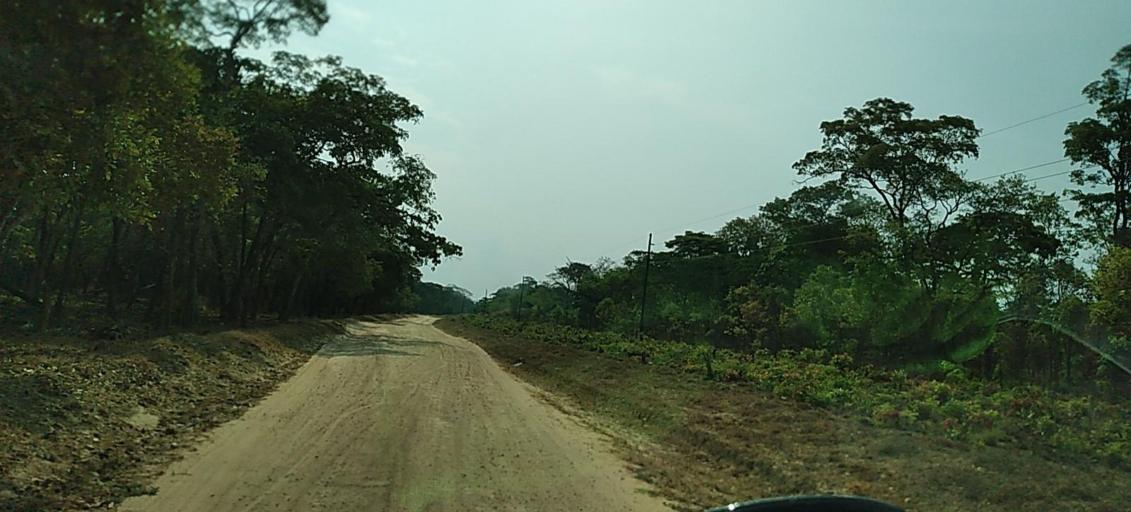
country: ZM
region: North-Western
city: Solwezi
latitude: -12.6813
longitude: 26.3828
